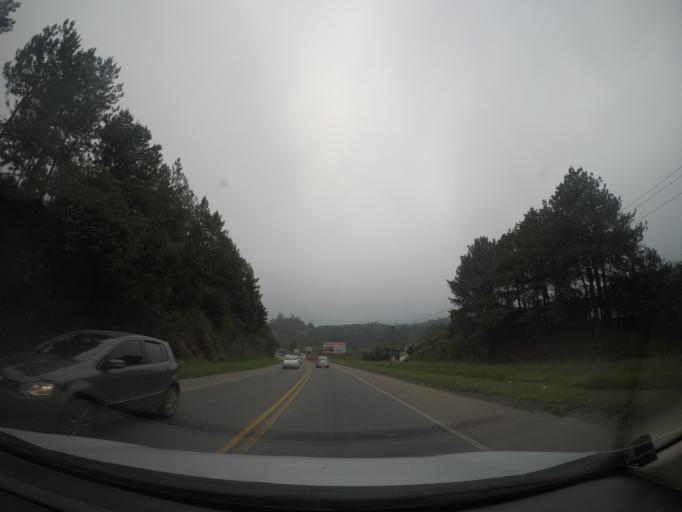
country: BR
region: Parana
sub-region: Almirante Tamandare
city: Almirante Tamandare
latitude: -25.3330
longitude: -49.2861
